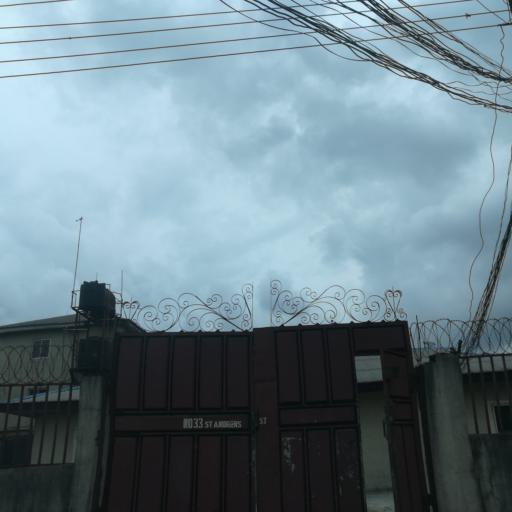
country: NG
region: Rivers
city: Port Harcourt
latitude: 4.8322
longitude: 7.0326
